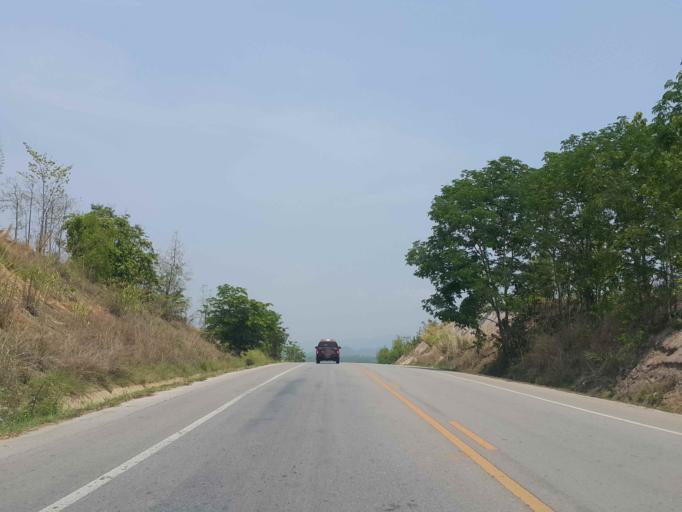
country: TH
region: Chiang Mai
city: Mae Taeng
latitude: 19.0818
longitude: 98.9152
